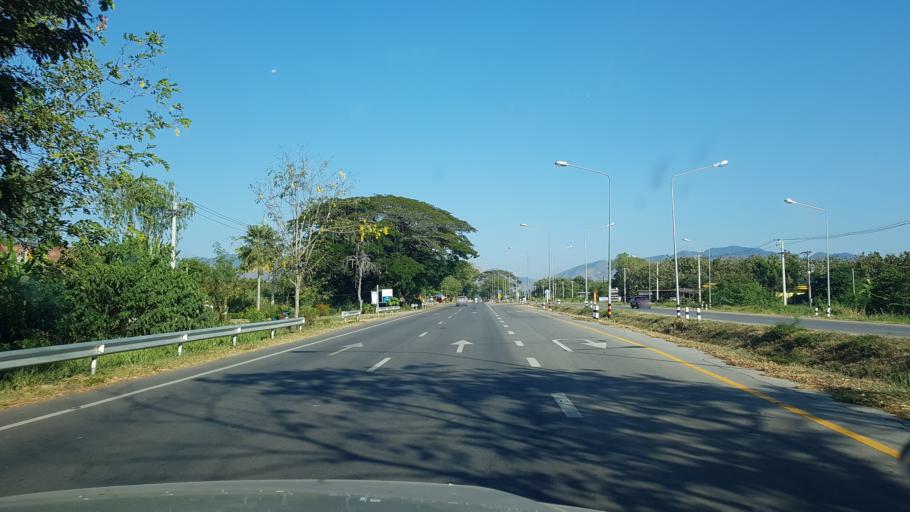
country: TH
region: Phetchabun
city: Lom Sak
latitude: 16.7277
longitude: 101.2694
